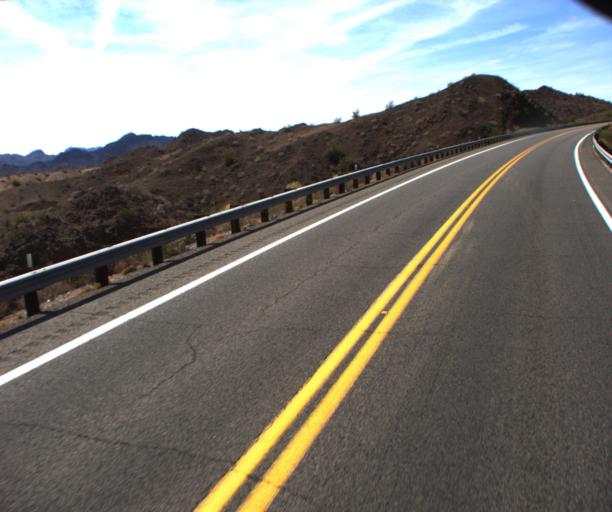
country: US
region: Arizona
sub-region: La Paz County
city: Cienega Springs
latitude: 34.3054
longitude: -114.0974
